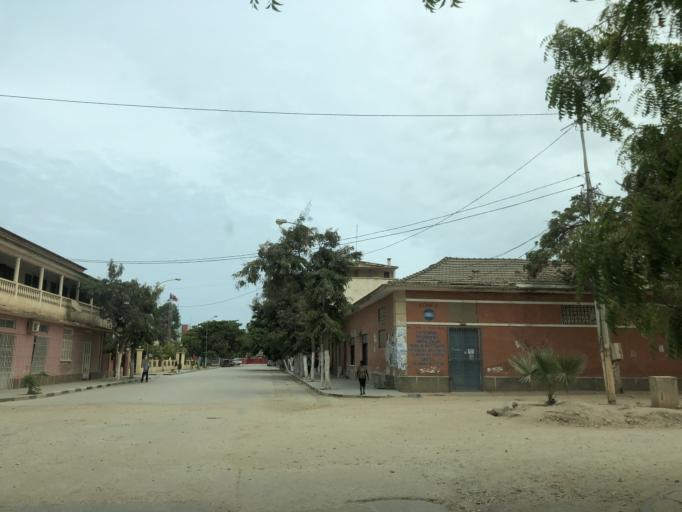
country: AO
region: Cuanza Sul
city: Sumbe
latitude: -11.2021
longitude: 13.8420
